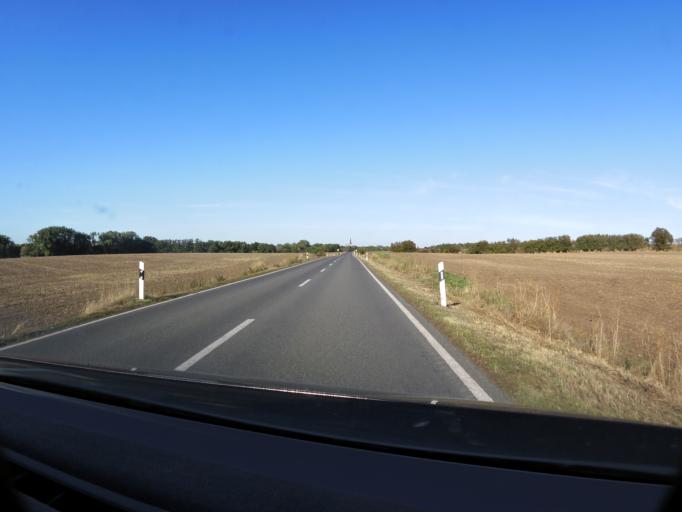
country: DE
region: Saxony-Anhalt
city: Groeningen
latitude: 51.9235
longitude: 11.1989
